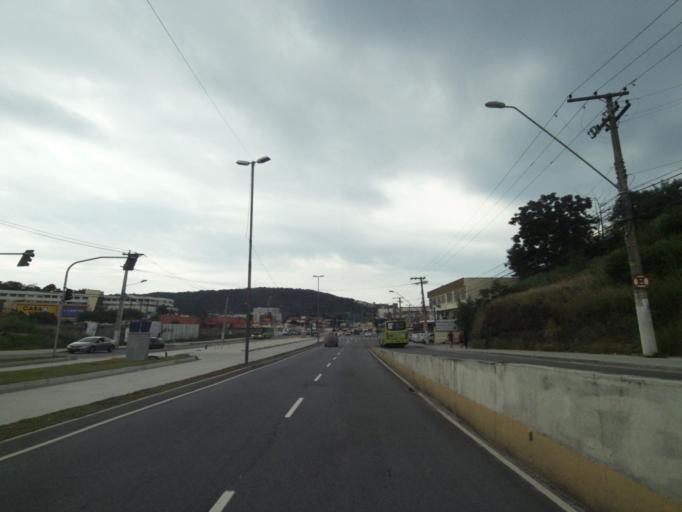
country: BR
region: Rio de Janeiro
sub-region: Niteroi
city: Niteroi
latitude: -22.9401
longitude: -43.0587
